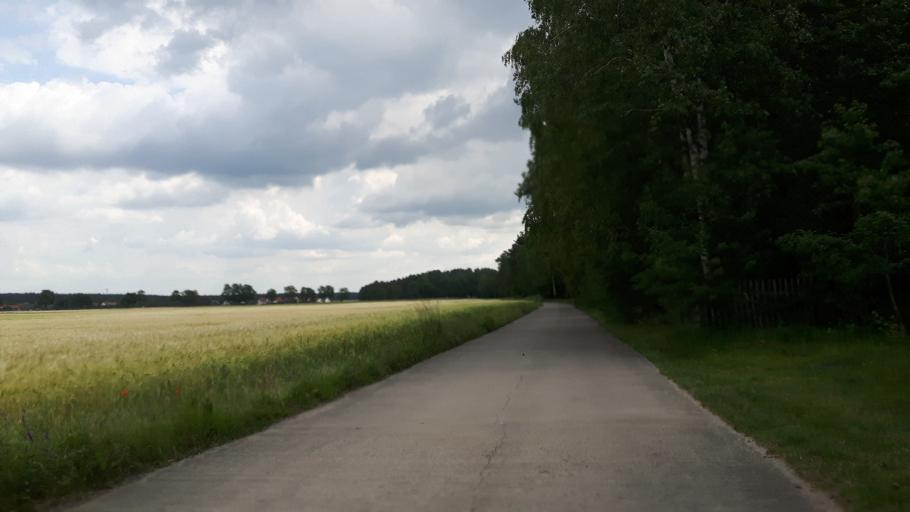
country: DE
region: Saxony-Anhalt
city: Schlaitz
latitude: 51.6518
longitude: 12.4295
